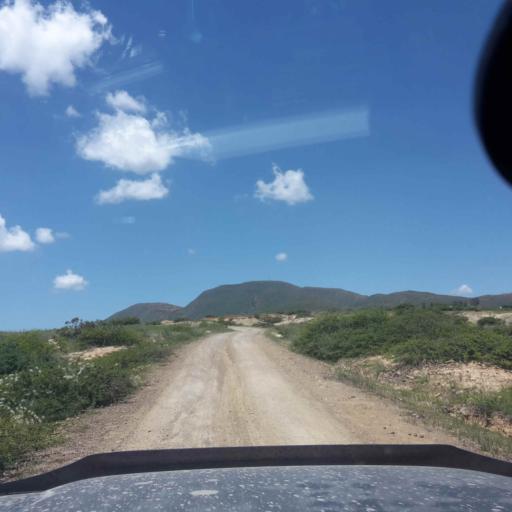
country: BO
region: Cochabamba
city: Totora
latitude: -17.7710
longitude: -65.2574
